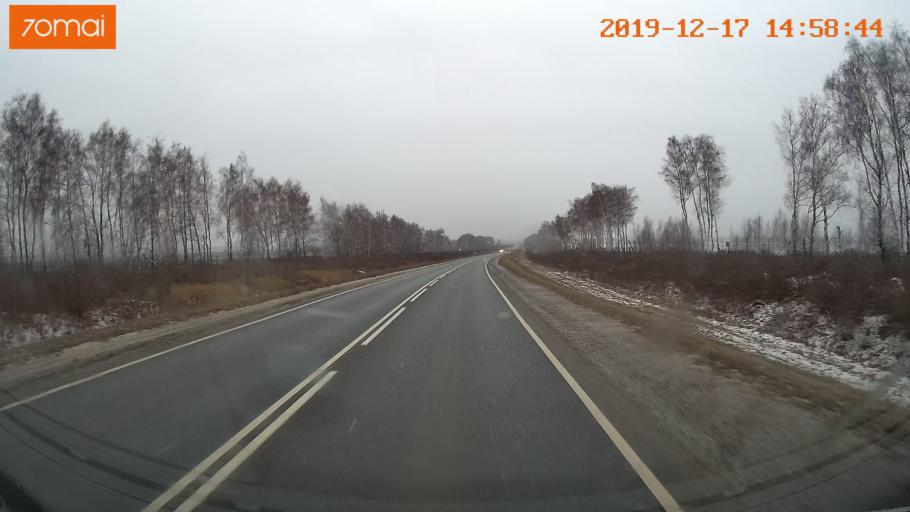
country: RU
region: Rjazan
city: Zakharovo
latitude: 54.3115
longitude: 39.2184
